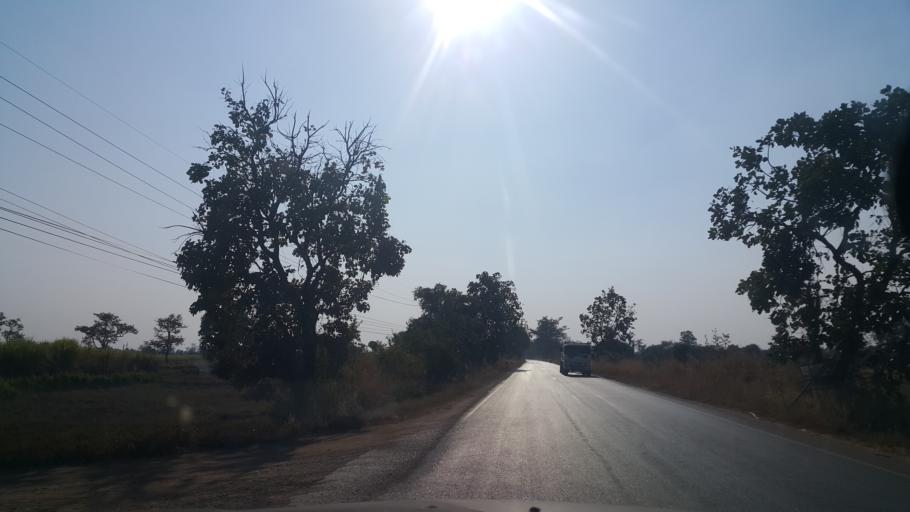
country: TH
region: Nakhon Ratchasima
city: Phimai
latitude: 15.1885
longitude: 102.4253
